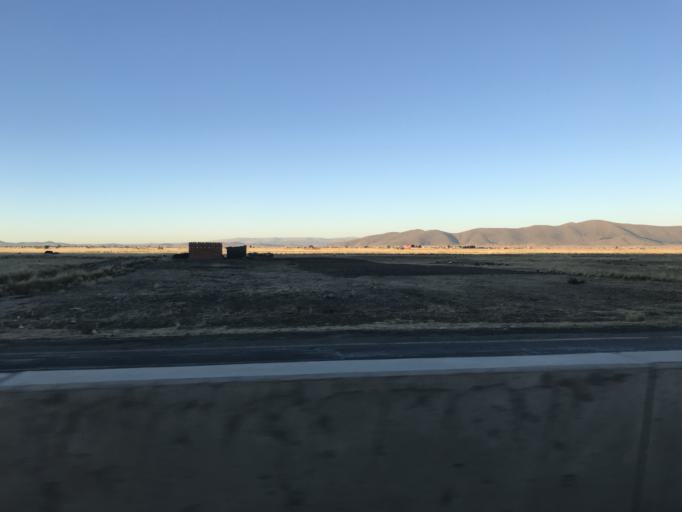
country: BO
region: La Paz
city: Batallas
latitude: -16.2988
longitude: -68.5170
